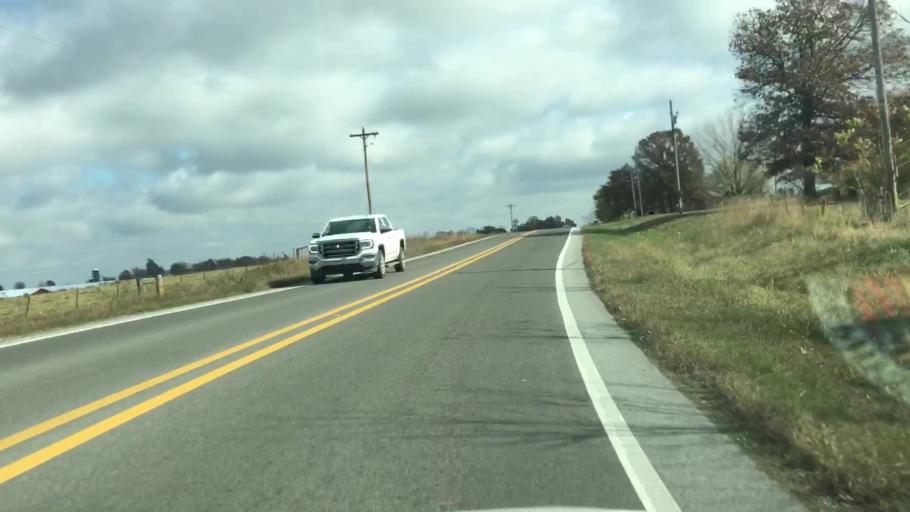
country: US
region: Arkansas
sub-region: Benton County
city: Gentry
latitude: 36.2618
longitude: -94.3677
